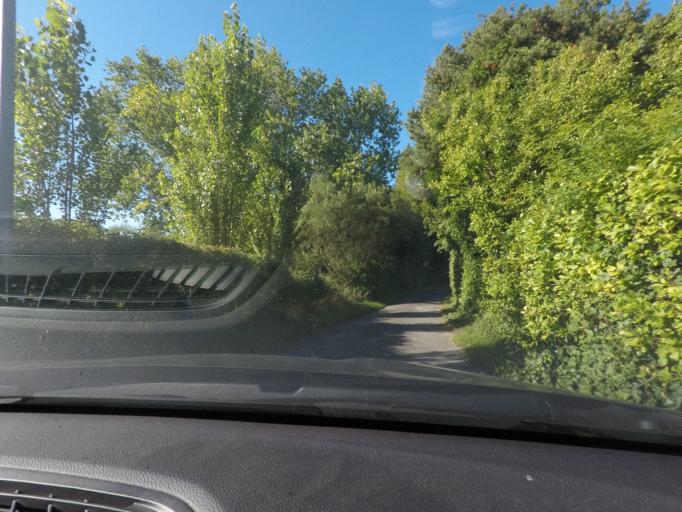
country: DK
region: Zealand
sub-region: Guldborgsund Kommune
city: Sakskobing
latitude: 54.9779
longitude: 11.5314
